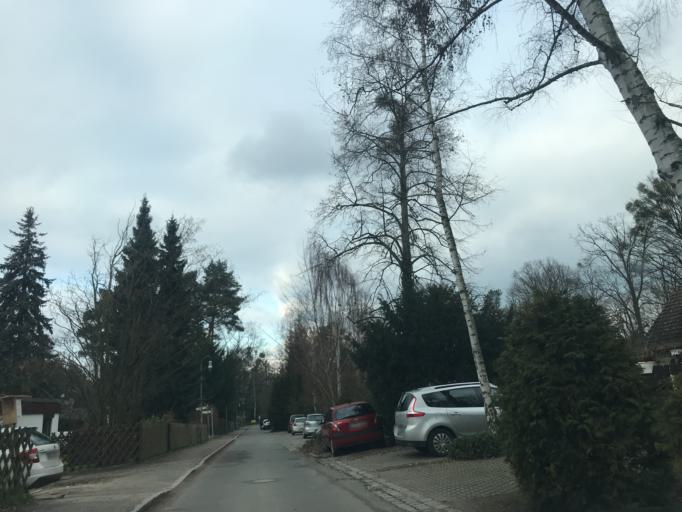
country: DE
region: Berlin
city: Kladow
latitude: 52.4512
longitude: 13.1315
